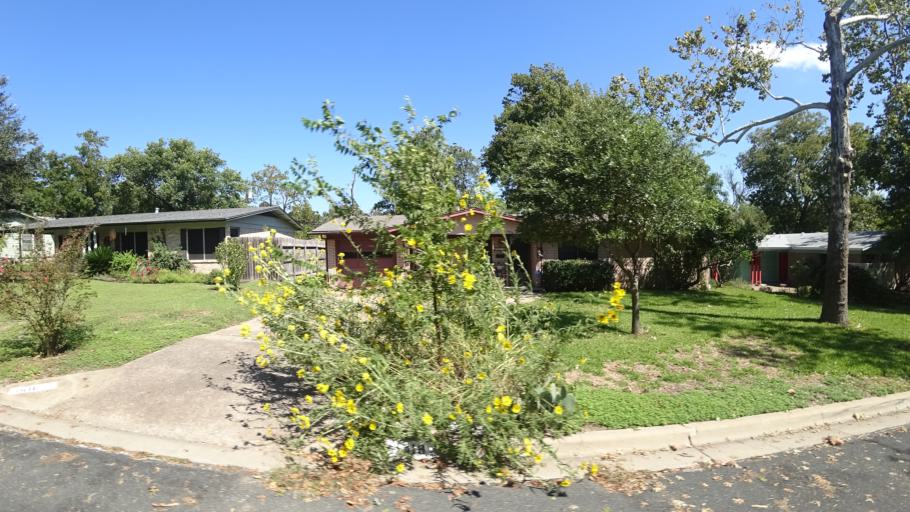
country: US
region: Texas
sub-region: Travis County
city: Austin
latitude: 30.3151
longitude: -97.6964
